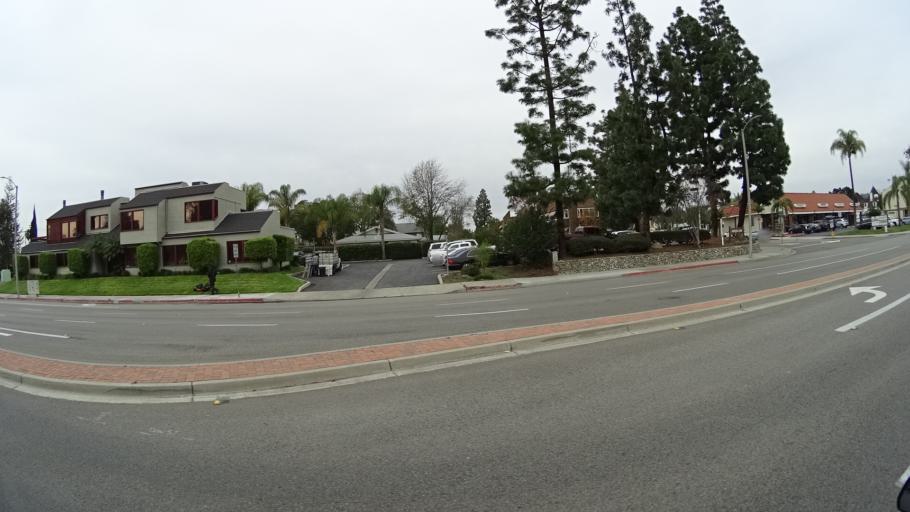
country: US
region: California
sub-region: Orange County
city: Tustin
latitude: 33.7482
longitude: -117.8136
